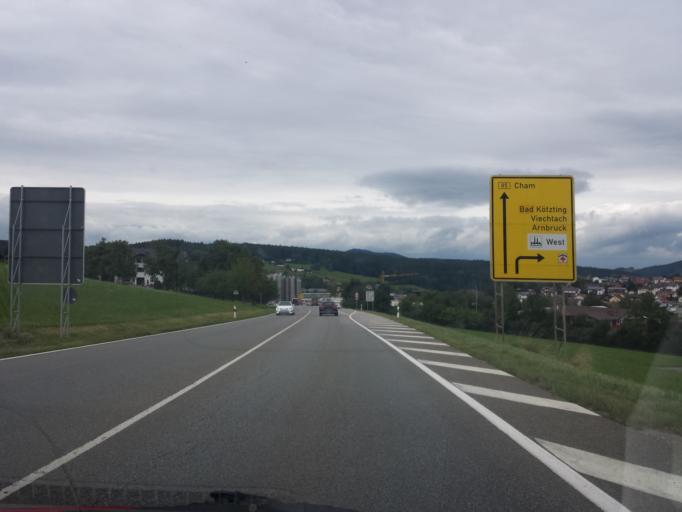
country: DE
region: Bavaria
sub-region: Lower Bavaria
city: Viechtach
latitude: 49.0763
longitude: 12.8778
